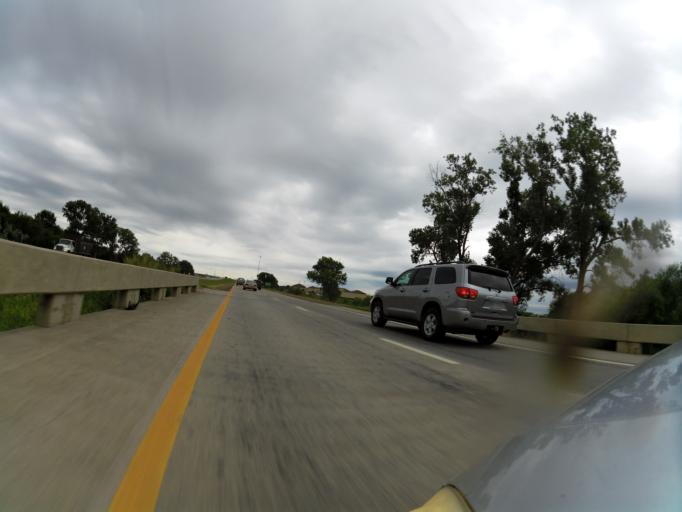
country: US
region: Kansas
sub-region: Sedgwick County
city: Maize
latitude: 37.7596
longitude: -97.4342
